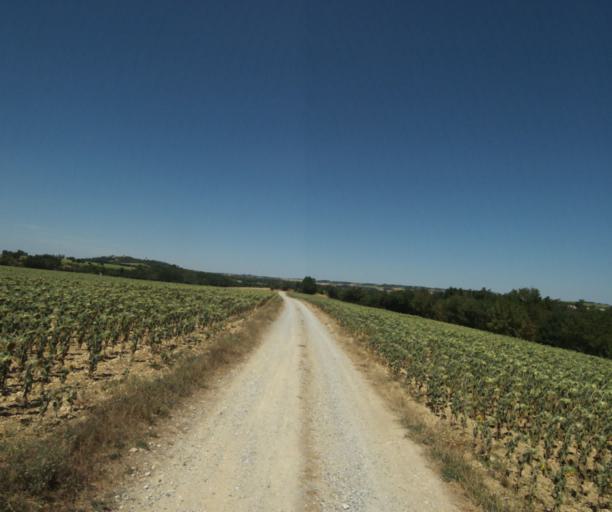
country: FR
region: Midi-Pyrenees
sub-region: Departement de la Haute-Garonne
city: Saint-Felix-Lauragais
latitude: 43.4718
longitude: 1.9183
